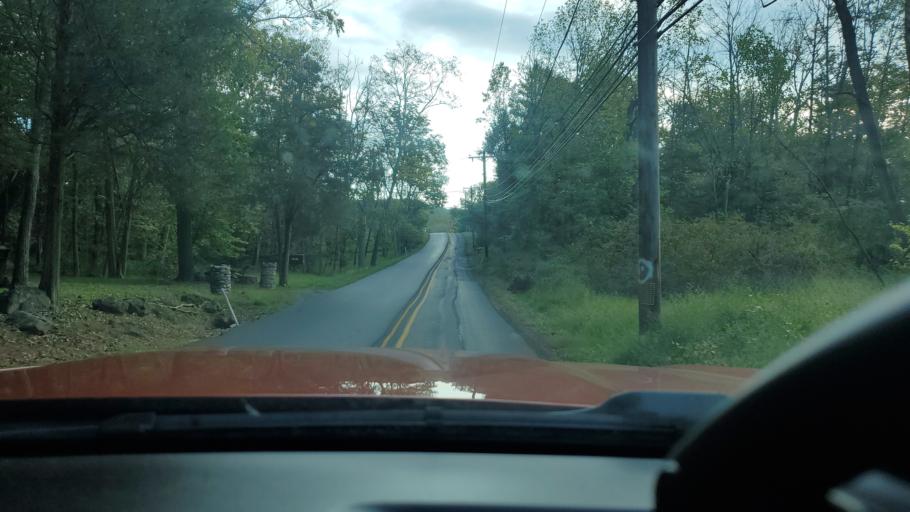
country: US
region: Pennsylvania
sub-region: Montgomery County
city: Woxall
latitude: 40.3228
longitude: -75.4854
